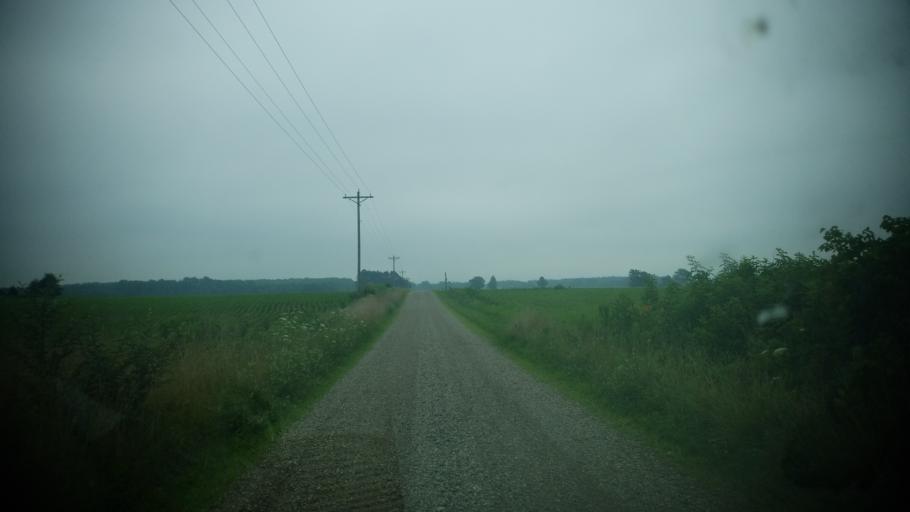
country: US
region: Illinois
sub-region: Clay County
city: Flora
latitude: 38.5880
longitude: -88.3740
